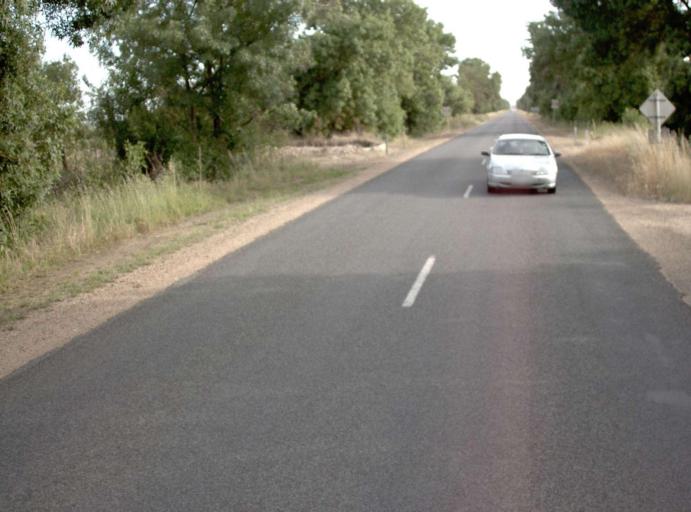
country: AU
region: Victoria
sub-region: Wellington
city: Heyfield
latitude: -37.9666
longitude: 146.8910
